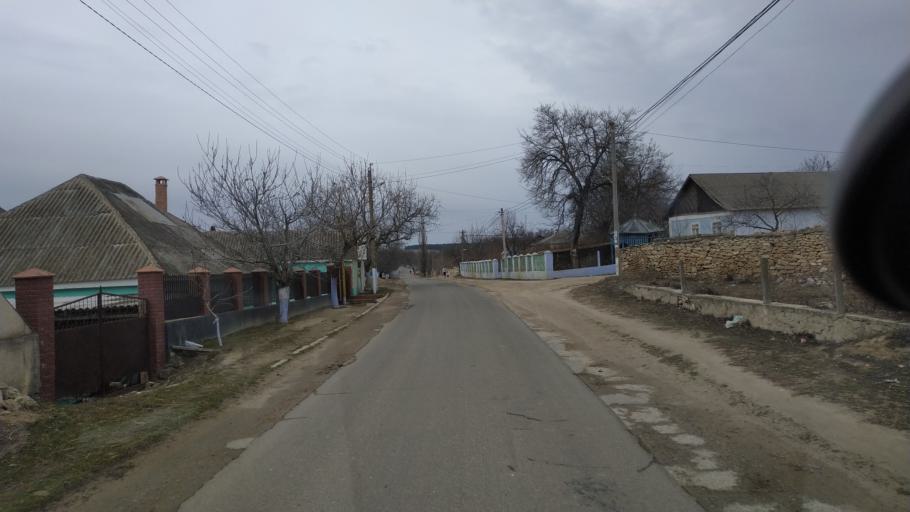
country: MD
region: Telenesti
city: Cocieri
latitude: 47.2687
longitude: 29.0674
